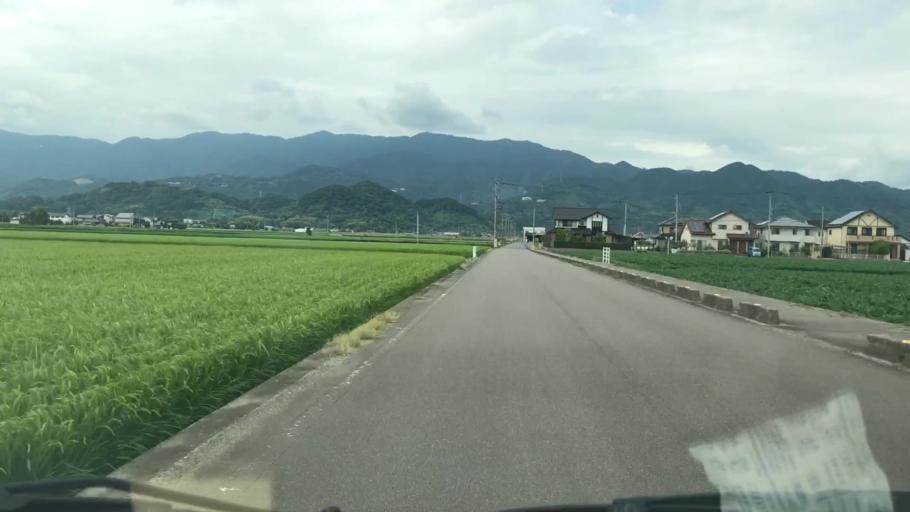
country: JP
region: Saga Prefecture
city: Saga-shi
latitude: 33.2843
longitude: 130.2257
